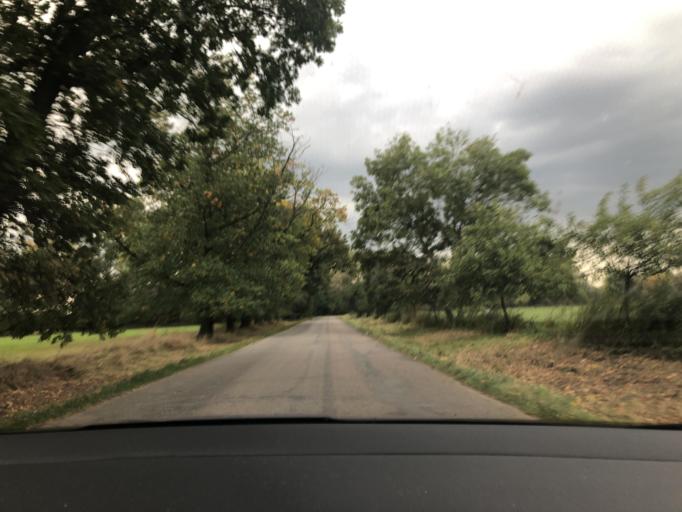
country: CZ
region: Pardubicky
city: Chvaletice
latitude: 50.0497
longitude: 15.4338
